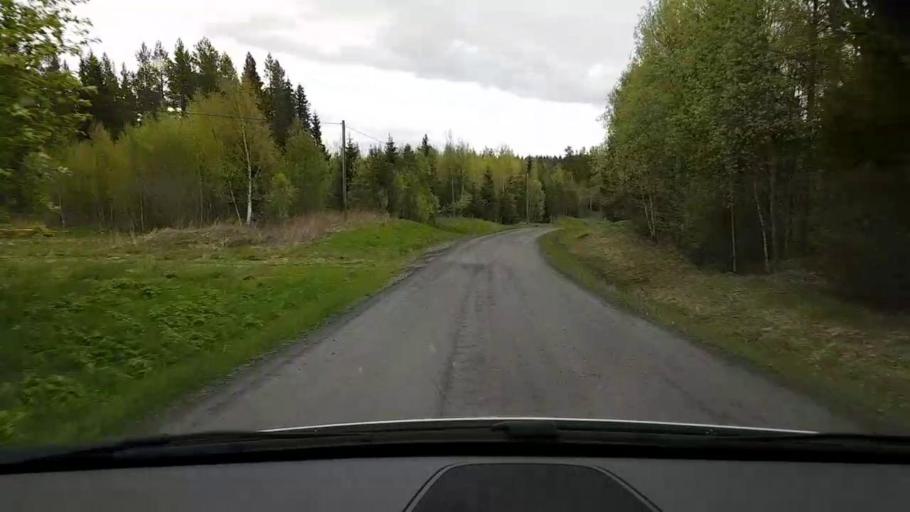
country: SE
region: Jaemtland
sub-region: Krokoms Kommun
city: Valla
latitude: 63.3051
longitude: 13.9459
